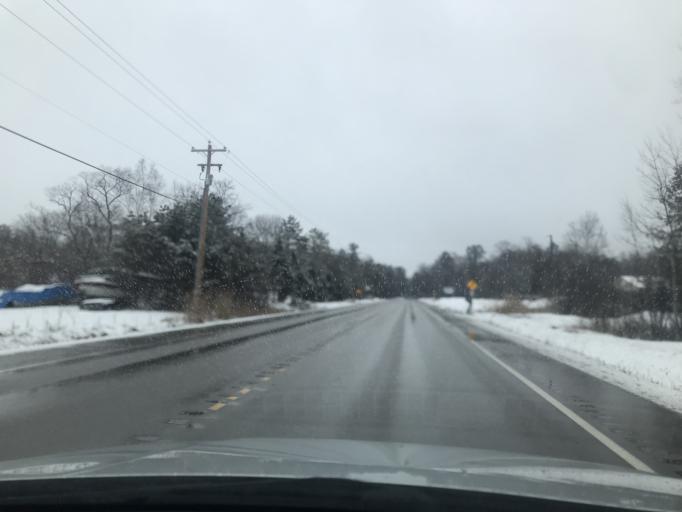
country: US
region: Wisconsin
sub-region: Marinette County
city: Marinette
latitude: 45.1114
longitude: -87.6708
